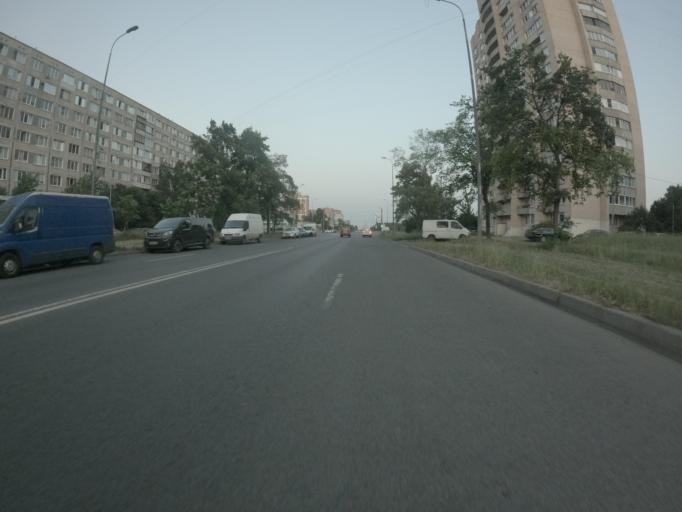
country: RU
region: St.-Petersburg
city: Krasnogvargeisky
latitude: 59.9163
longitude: 30.4839
